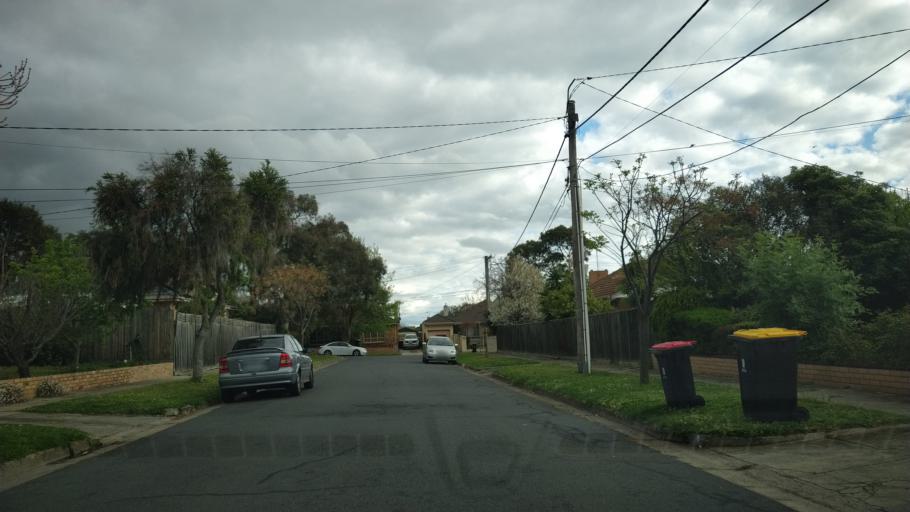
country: AU
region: Victoria
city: Highett
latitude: -37.9524
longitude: 145.0665
